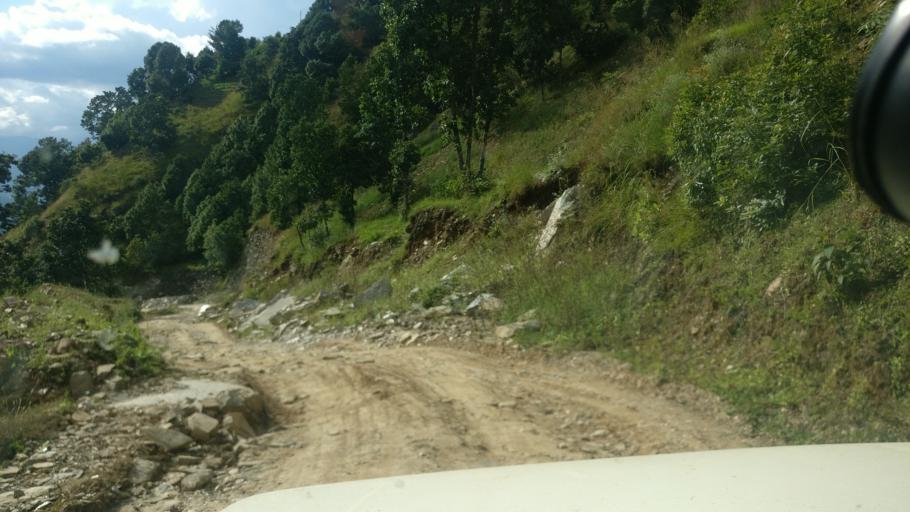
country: NP
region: Western Region
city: Baglung
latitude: 28.2644
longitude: 83.6454
